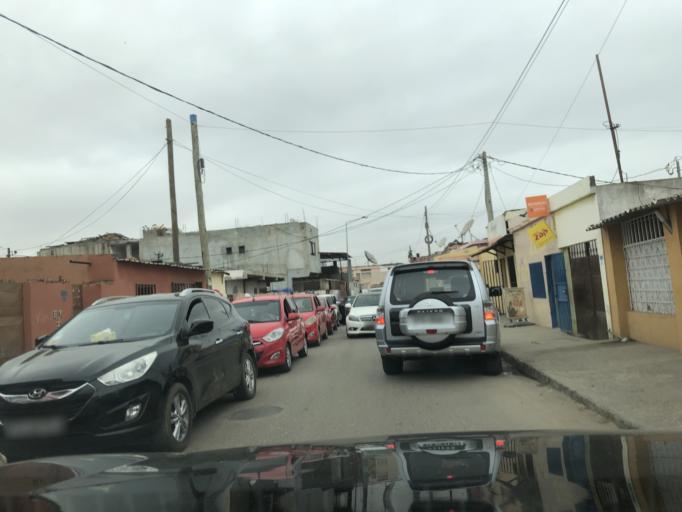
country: AO
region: Luanda
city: Luanda
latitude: -8.8416
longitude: 13.2302
